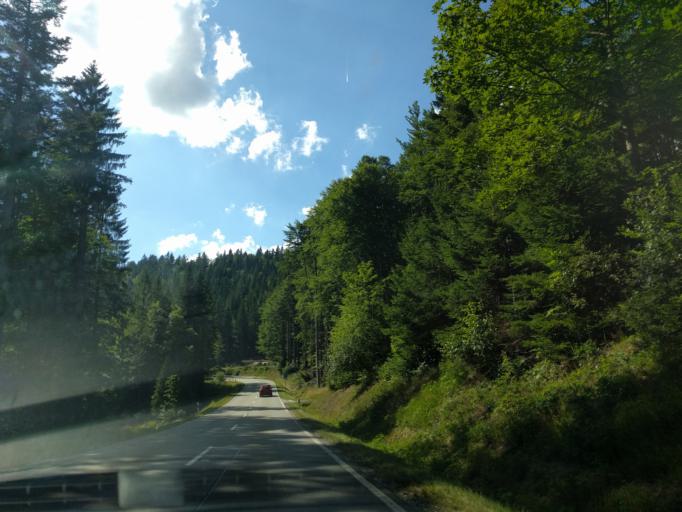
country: DE
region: Bavaria
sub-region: Lower Bavaria
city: Bodenmais
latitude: 49.0701
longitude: 13.1418
